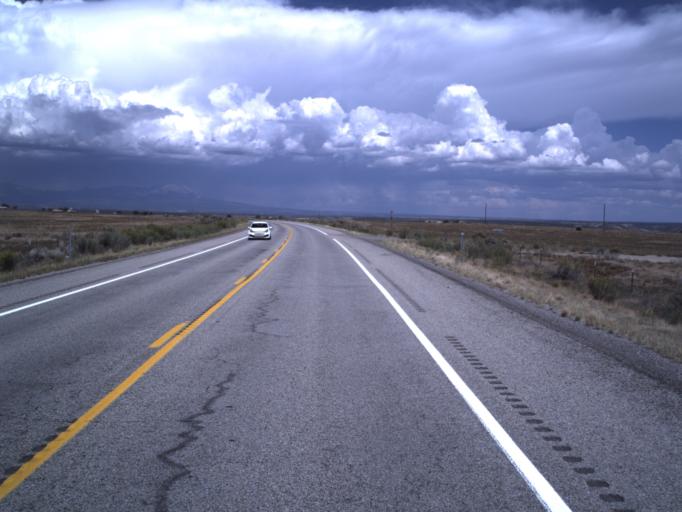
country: US
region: Utah
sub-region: San Juan County
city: Blanding
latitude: 37.4448
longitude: -109.4676
